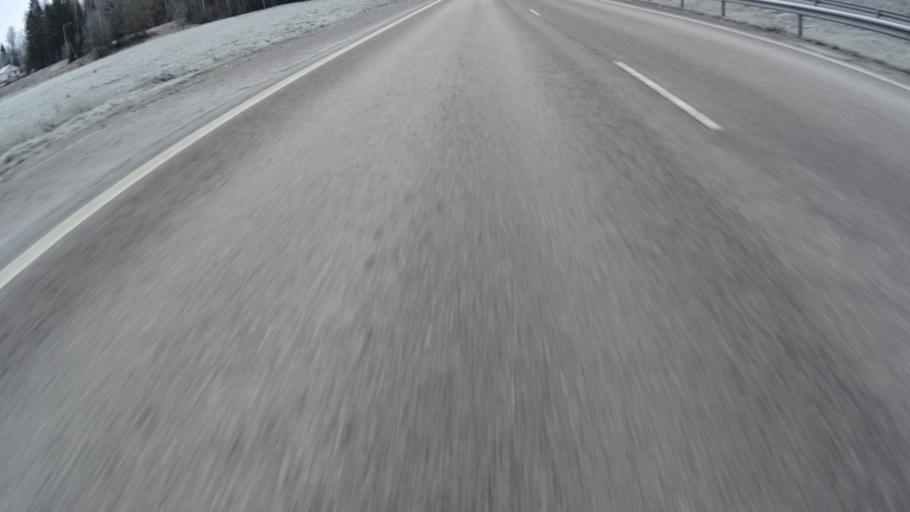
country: FI
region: Uusimaa
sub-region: Helsinki
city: Nurmijaervi
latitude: 60.3398
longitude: 24.8164
